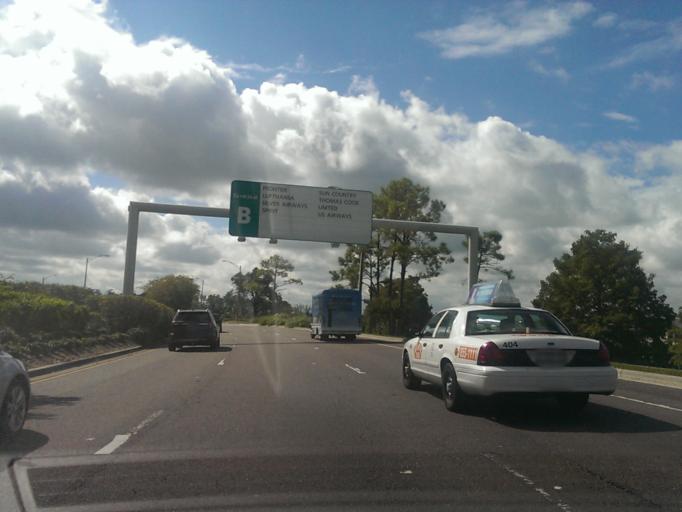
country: US
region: Florida
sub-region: Orange County
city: Taft
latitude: 28.4299
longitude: -81.3113
